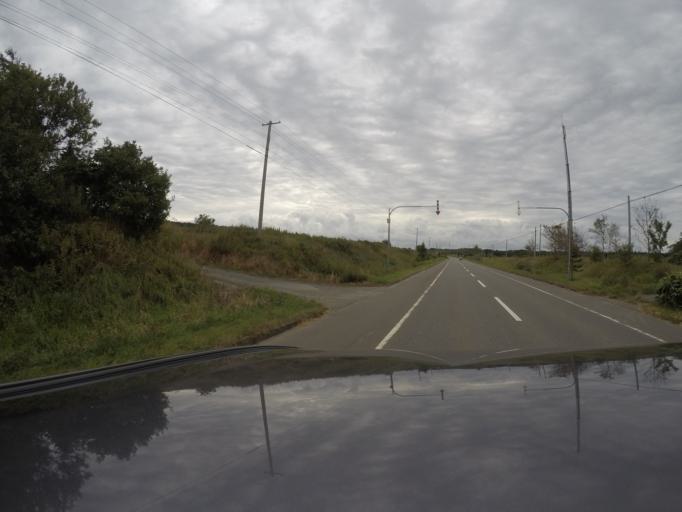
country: JP
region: Hokkaido
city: Makubetsu
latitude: 45.1825
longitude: 141.7420
